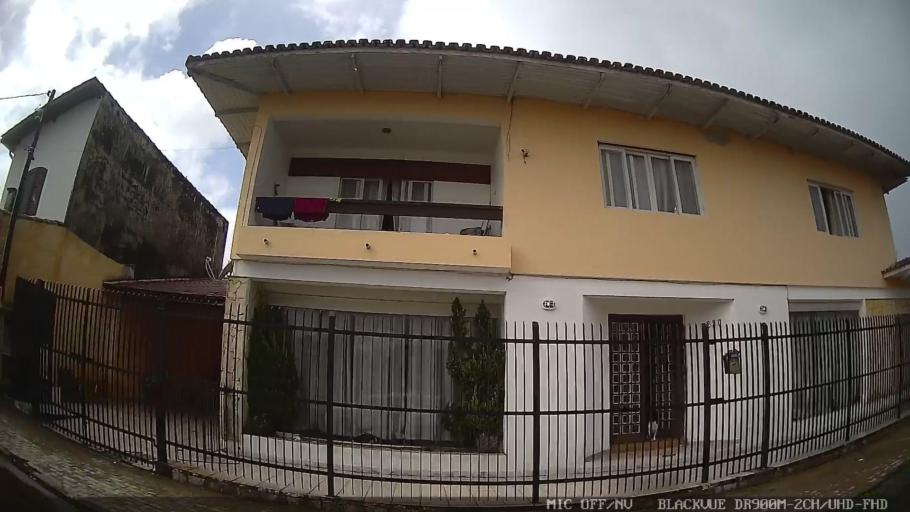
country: BR
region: Sao Paulo
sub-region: Itanhaem
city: Itanhaem
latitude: -24.2015
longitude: -46.8235
